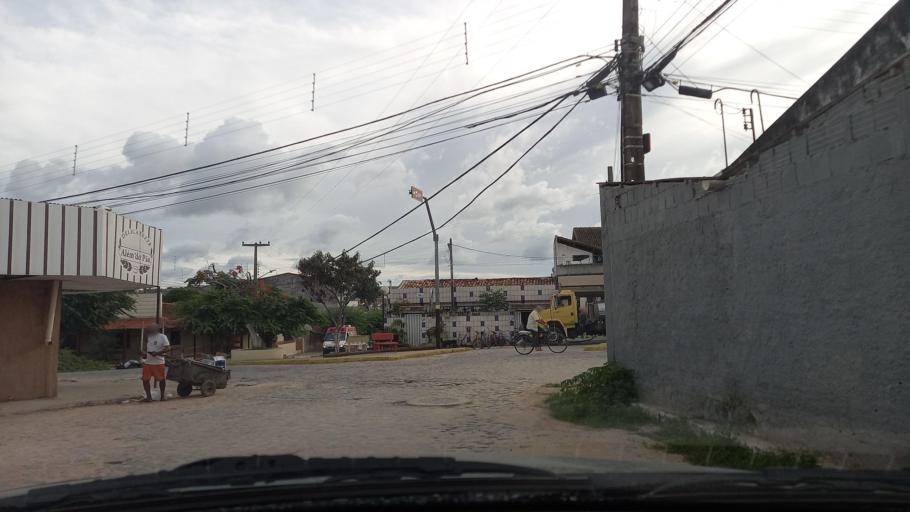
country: BR
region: Pernambuco
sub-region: Gravata
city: Gravata
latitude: -8.2026
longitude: -35.5621
